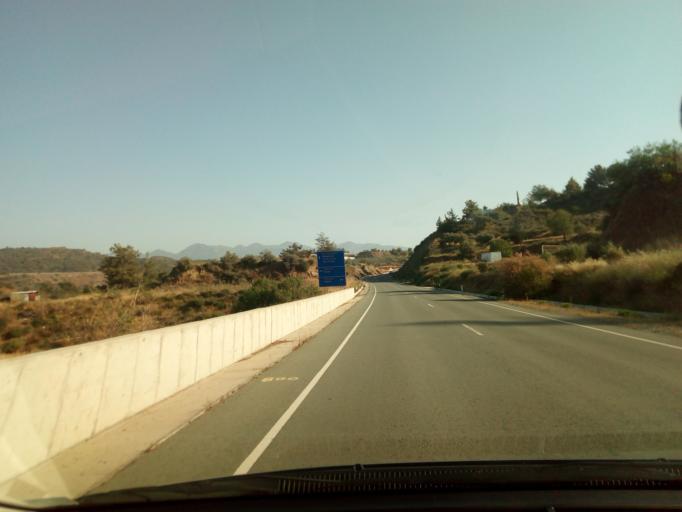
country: CY
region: Limassol
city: Parekklisha
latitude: 34.8126
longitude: 33.1511
